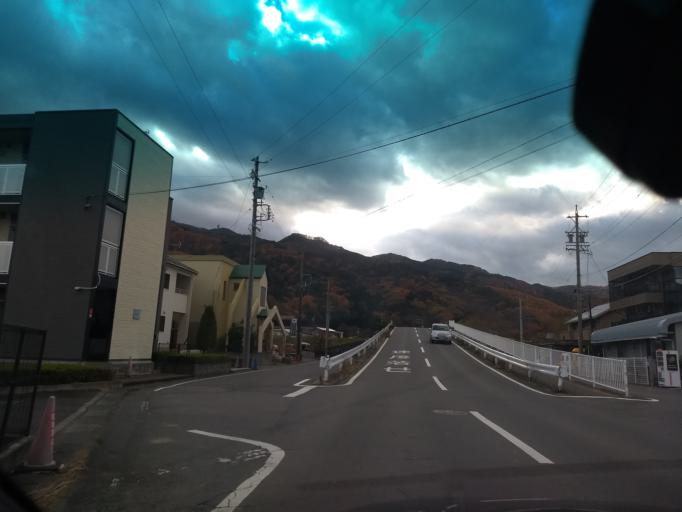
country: JP
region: Nagano
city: Chino
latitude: 36.0004
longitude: 138.1299
